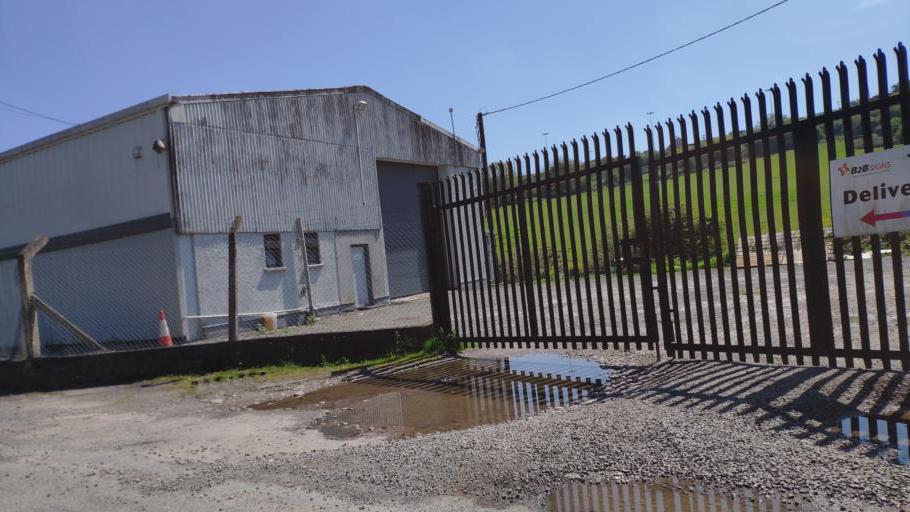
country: IE
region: Munster
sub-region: County Cork
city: Cork
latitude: 51.9199
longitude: -8.5029
